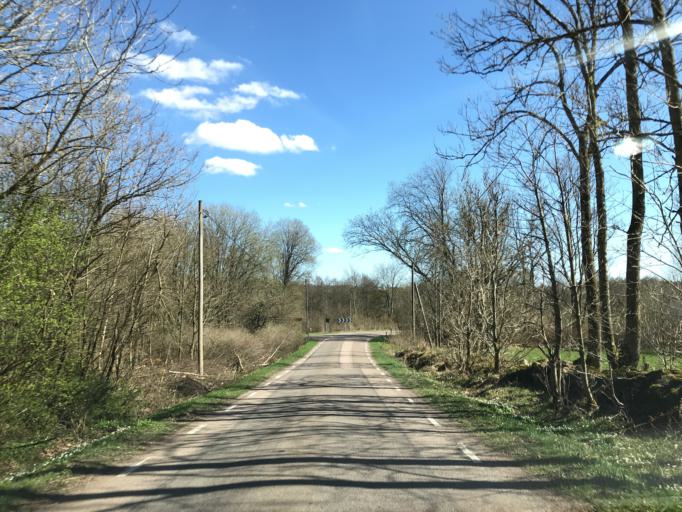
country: SE
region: Skane
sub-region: Svalovs Kommun
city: Kagerod
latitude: 56.0221
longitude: 13.1632
